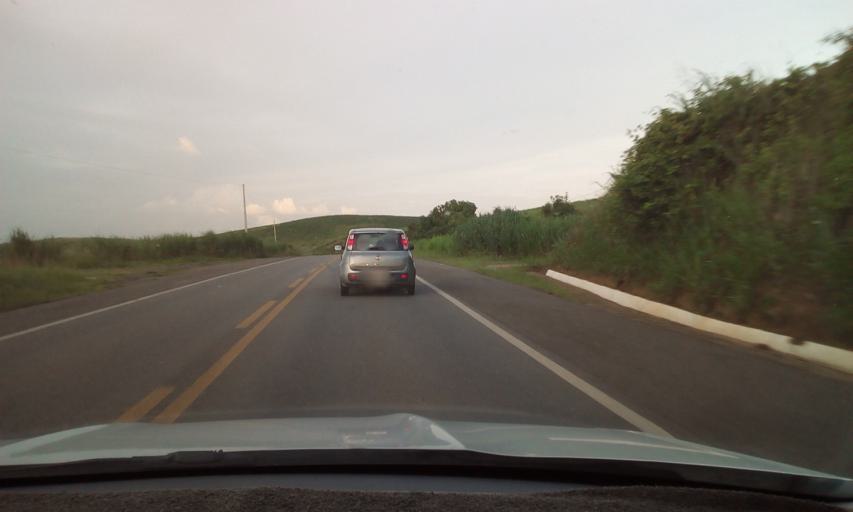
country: BR
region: Pernambuco
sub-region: Vicencia
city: Vicencia
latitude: -7.6263
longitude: -35.2435
